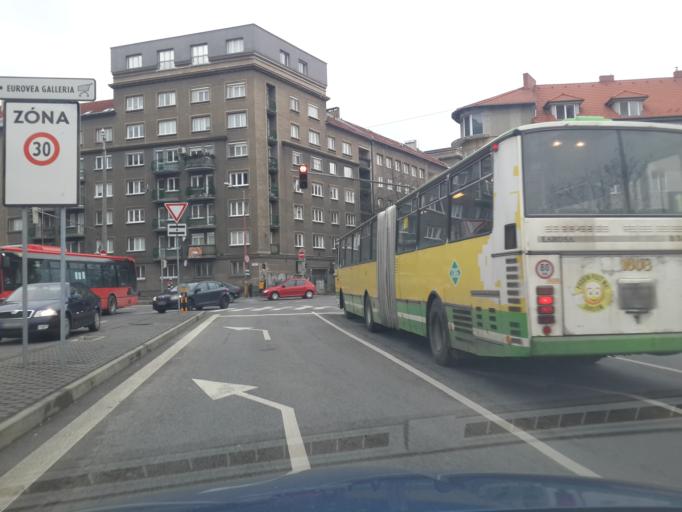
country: SK
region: Bratislavsky
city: Bratislava
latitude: 48.1429
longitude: 17.1223
